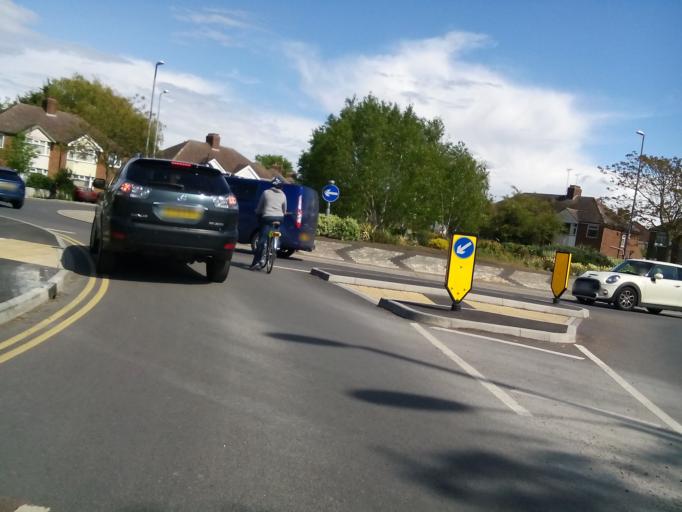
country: GB
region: England
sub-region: Cambridgeshire
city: Cambridge
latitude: 52.1925
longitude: 0.1539
